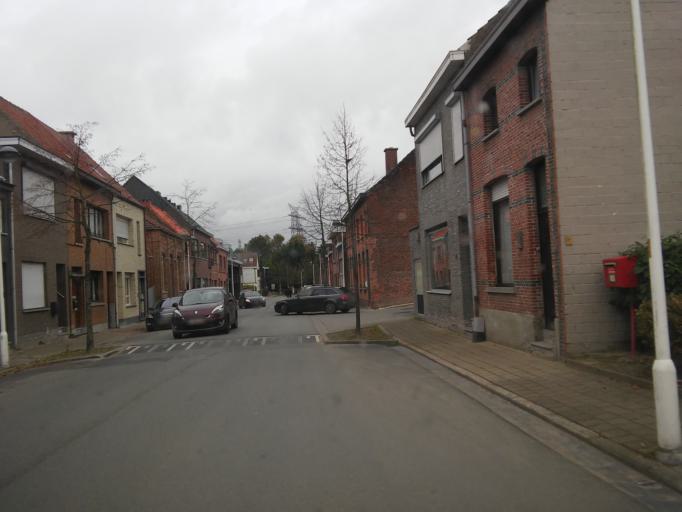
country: BE
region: Flanders
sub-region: Provincie Oost-Vlaanderen
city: Kruibeke
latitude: 51.1323
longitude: 4.2929
